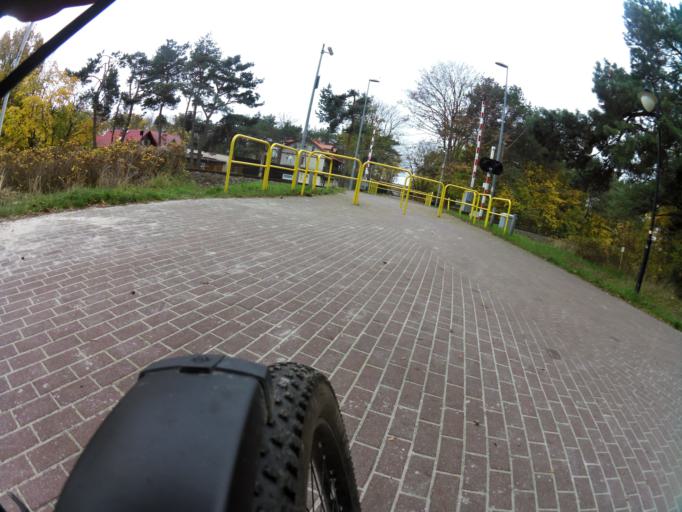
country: PL
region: Pomeranian Voivodeship
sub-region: Powiat pucki
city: Jastarnia
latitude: 54.6988
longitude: 18.6852
